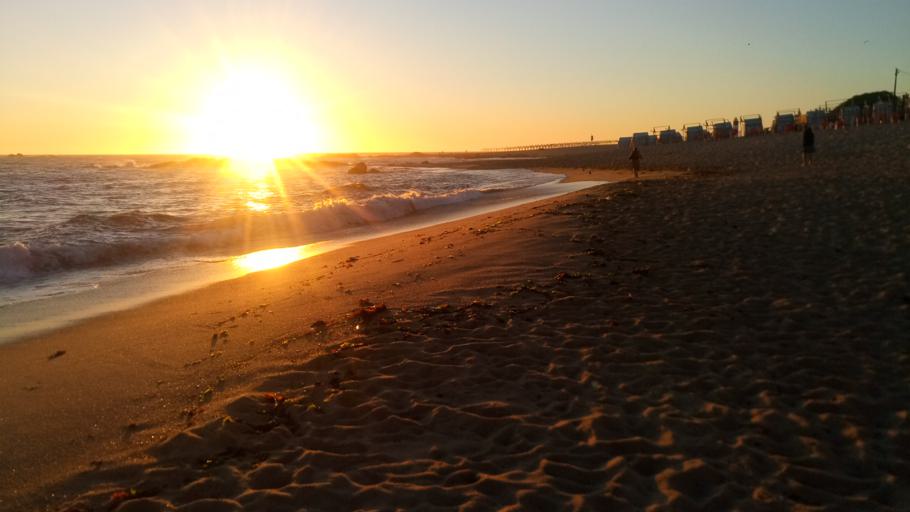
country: PT
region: Porto
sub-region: Povoa de Varzim
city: Aver-o-Mar
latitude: 41.3937
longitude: -8.7771
